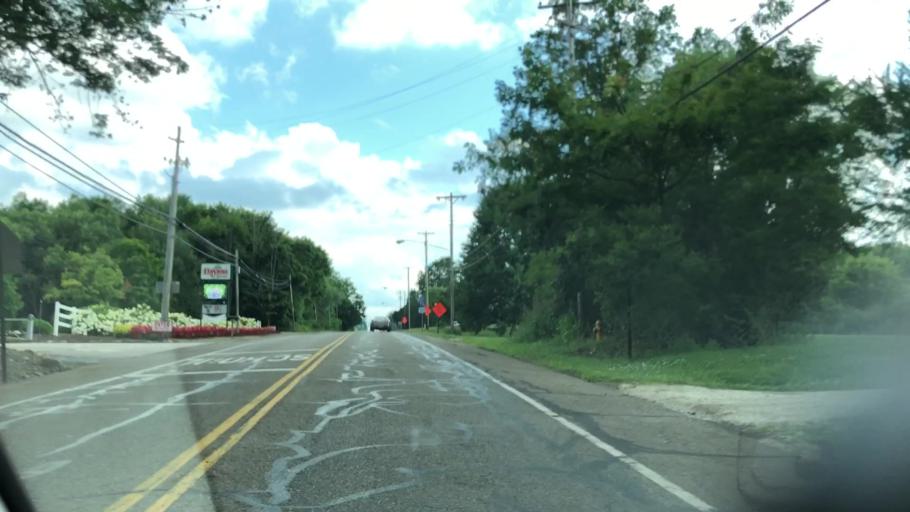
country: US
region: Ohio
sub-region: Summit County
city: Norton
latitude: 41.0446
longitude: -81.6378
